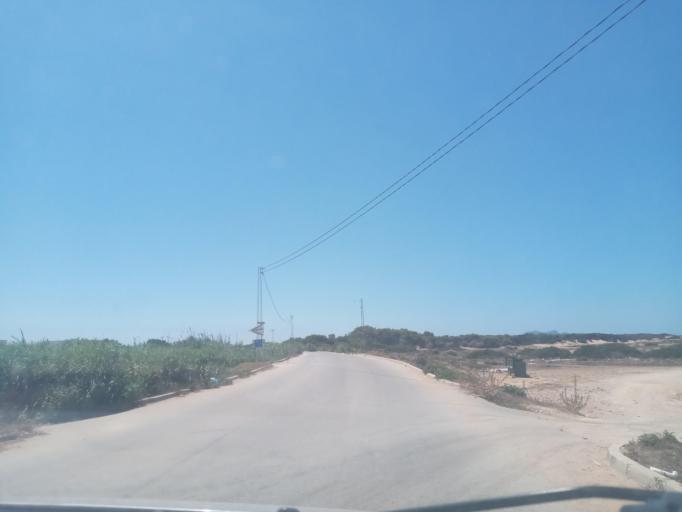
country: TN
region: Nabul
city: El Haouaria
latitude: 37.0495
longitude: 10.9692
